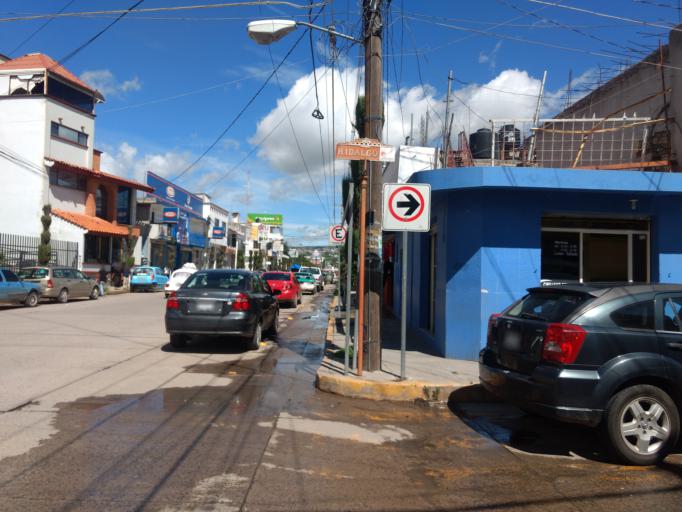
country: MX
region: Oaxaca
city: Ciudad de Huajuapam de Leon
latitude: 17.8035
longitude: -97.7769
